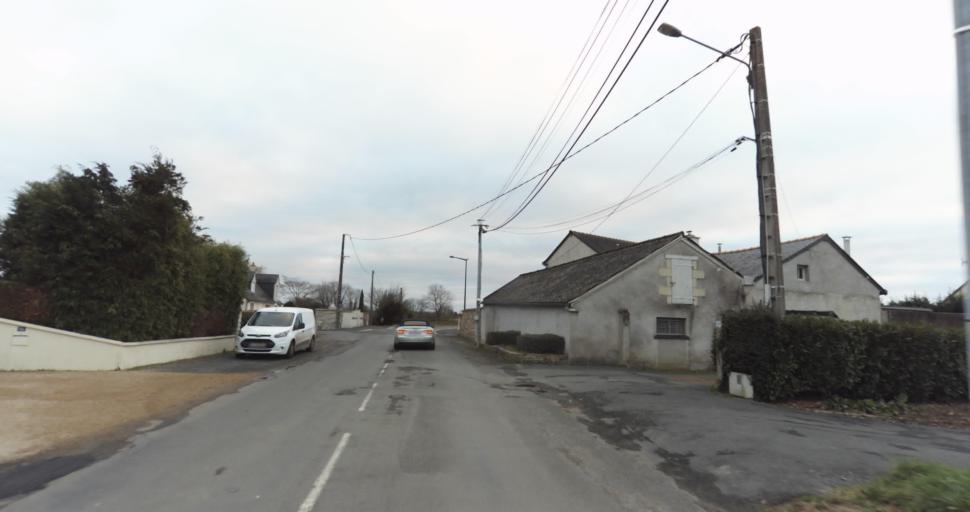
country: FR
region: Pays de la Loire
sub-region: Departement de Maine-et-Loire
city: Distre
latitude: 47.2469
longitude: -0.1083
